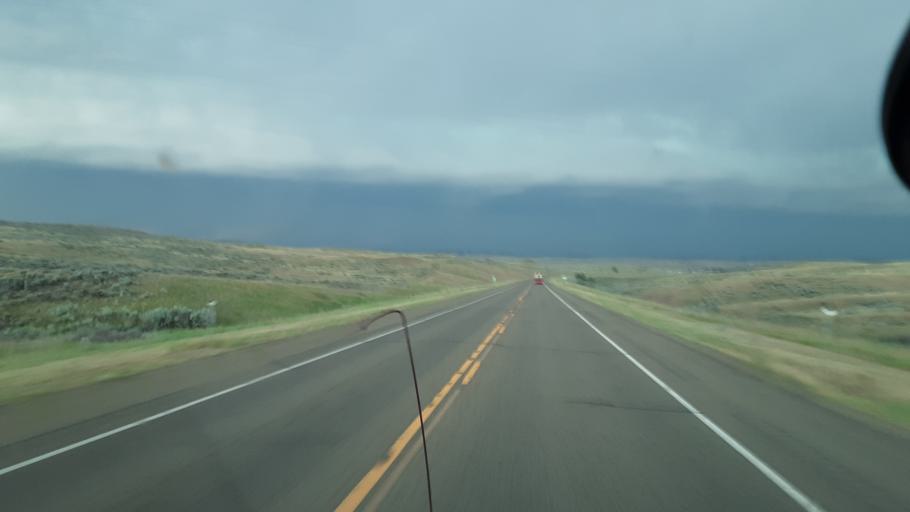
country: US
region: Montana
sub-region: Powder River County
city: Broadus
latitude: 45.4016
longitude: -105.3656
